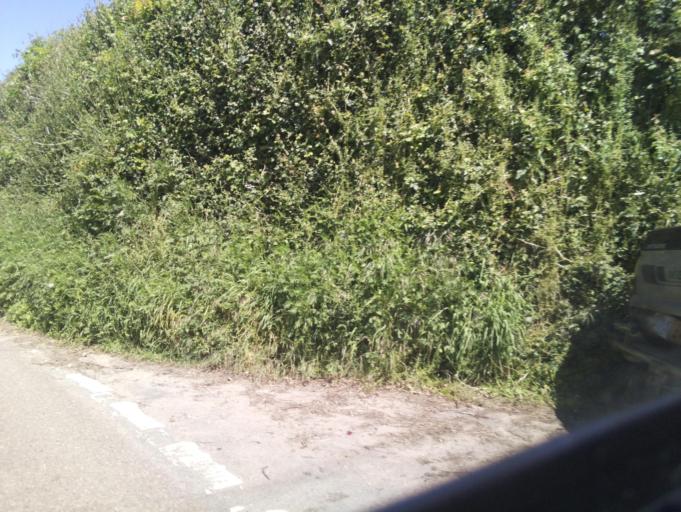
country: GB
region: England
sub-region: Devon
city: Newton Poppleford
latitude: 50.7200
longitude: -3.2829
